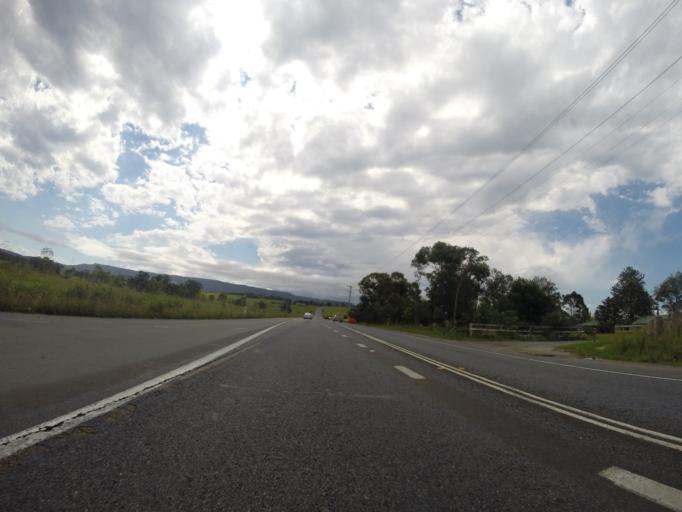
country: AU
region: New South Wales
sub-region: Shoalhaven Shire
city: Milton
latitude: -35.2994
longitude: 150.4300
